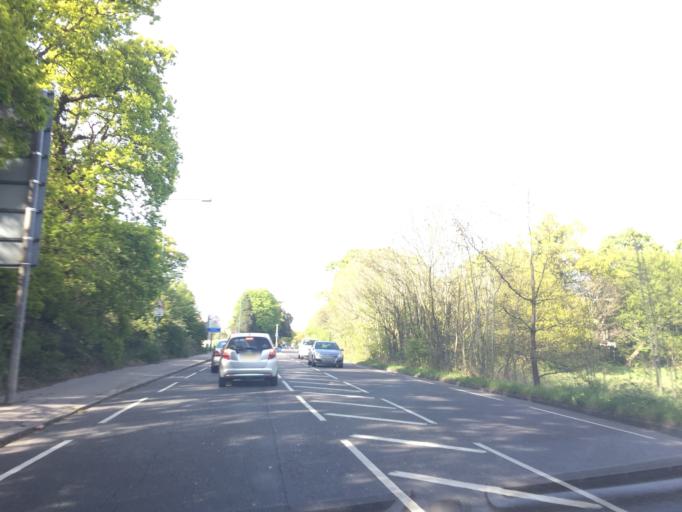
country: GB
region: England
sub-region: Greater London
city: Woodford Green
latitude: 51.5980
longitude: 0.0120
